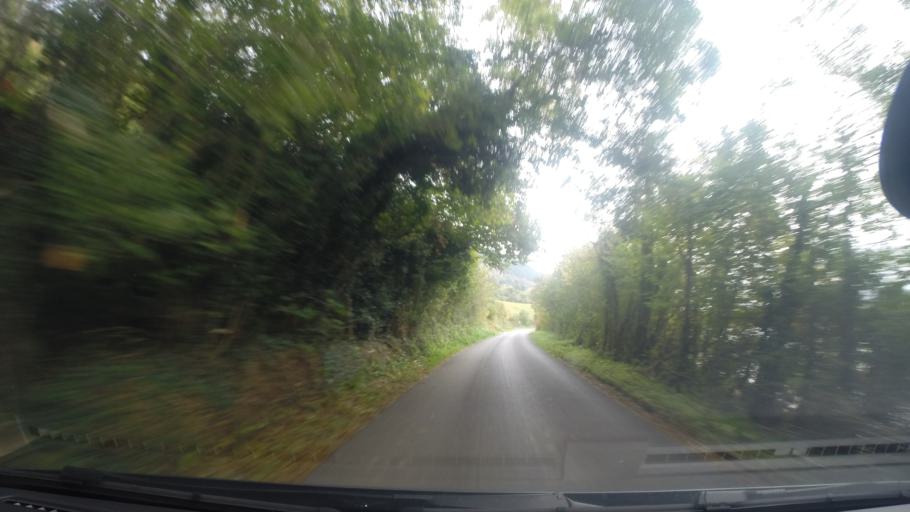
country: IE
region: Connaught
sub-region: Sligo
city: Sligo
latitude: 54.3408
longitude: -8.3764
